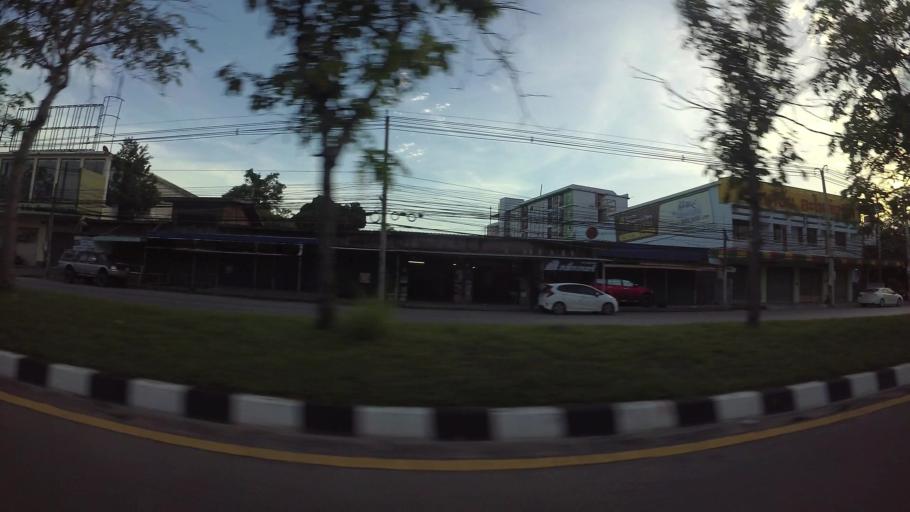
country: TH
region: Rayong
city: Rayong
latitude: 12.6765
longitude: 101.2883
